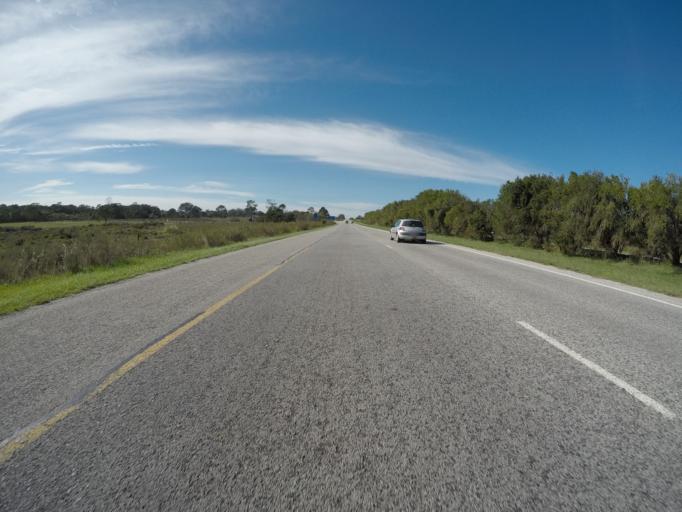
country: ZA
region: Eastern Cape
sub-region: Nelson Mandela Bay Metropolitan Municipality
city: Port Elizabeth
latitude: -33.9453
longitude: 25.3984
